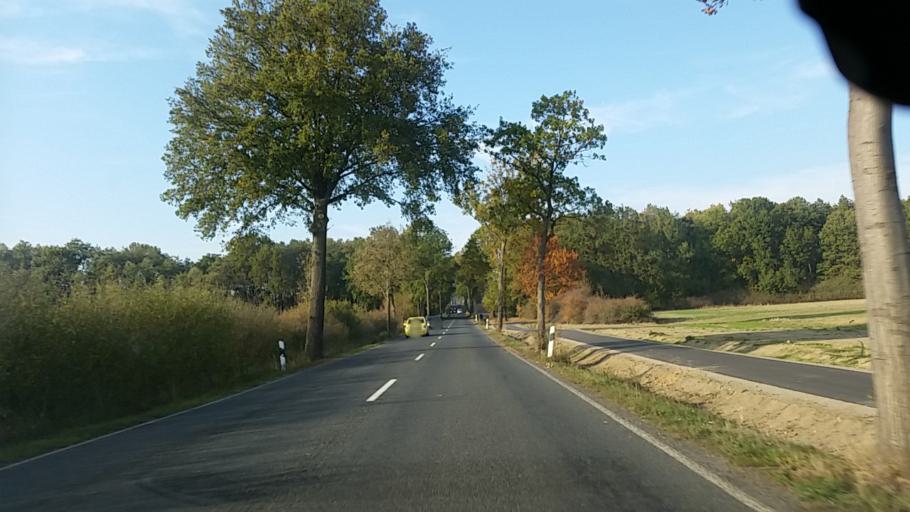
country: DE
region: Lower Saxony
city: Gross Twulpstedt
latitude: 52.3586
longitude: 10.8544
